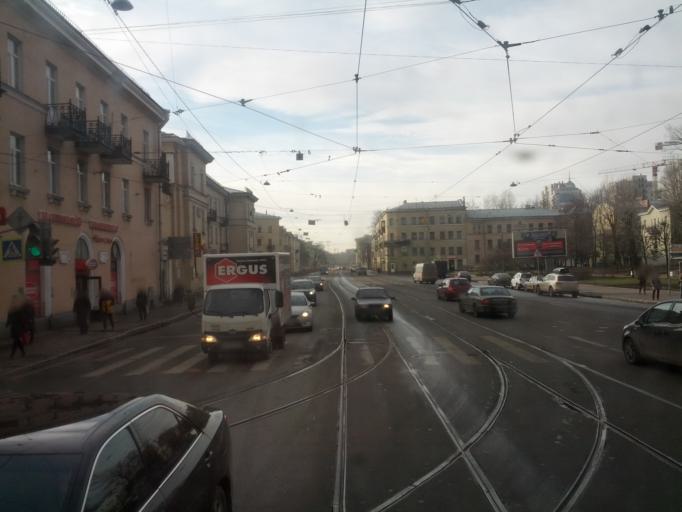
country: RU
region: Leningrad
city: Kalininskiy
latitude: 59.9534
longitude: 30.4150
